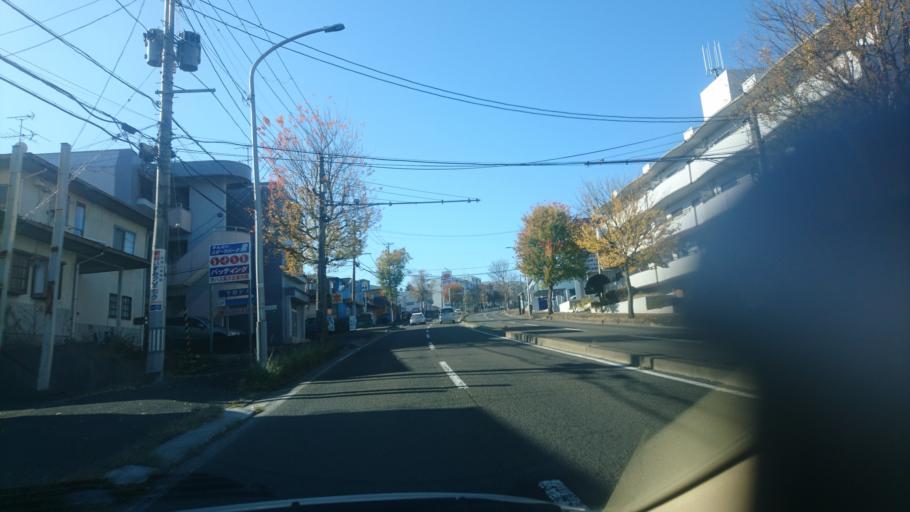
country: JP
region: Miyagi
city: Sendai-shi
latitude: 38.3083
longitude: 140.8414
